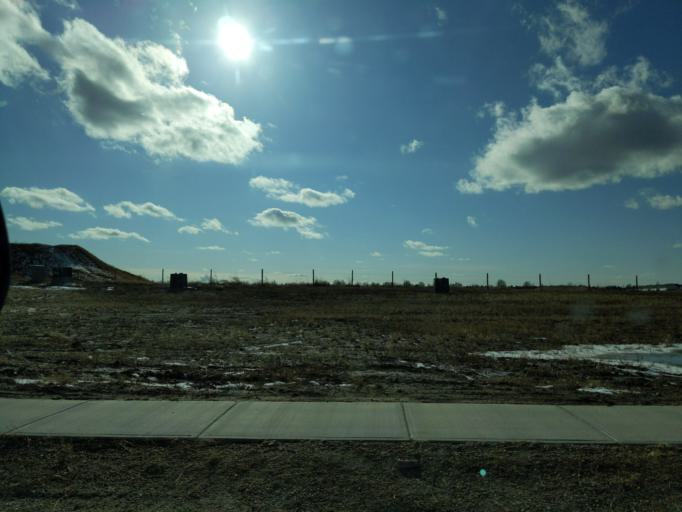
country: CA
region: Saskatchewan
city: Lloydminster
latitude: 53.2656
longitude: -109.9807
